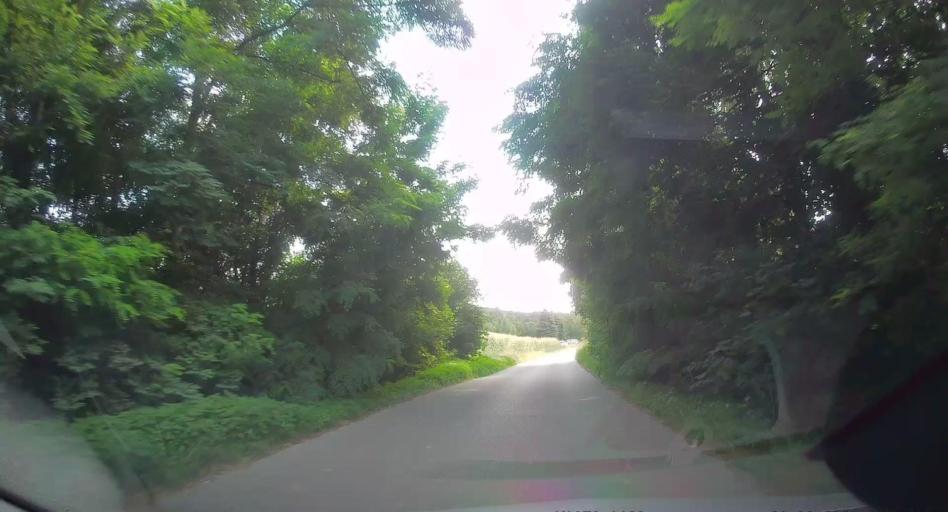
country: PL
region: Lesser Poland Voivodeship
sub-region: Powiat bochenski
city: Dziewin
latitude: 50.1544
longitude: 20.4633
